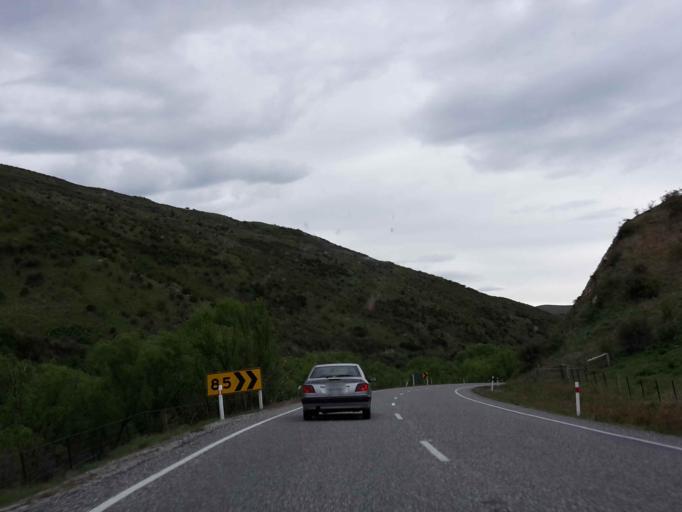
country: NZ
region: Otago
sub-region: Queenstown-Lakes District
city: Wanaka
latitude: -44.7298
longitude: 169.5069
